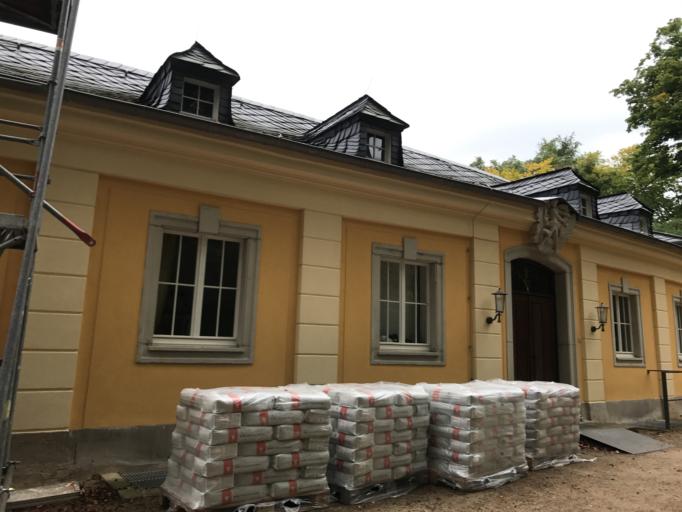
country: DE
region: Saxony
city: Dresden
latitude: 51.0326
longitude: 13.7710
